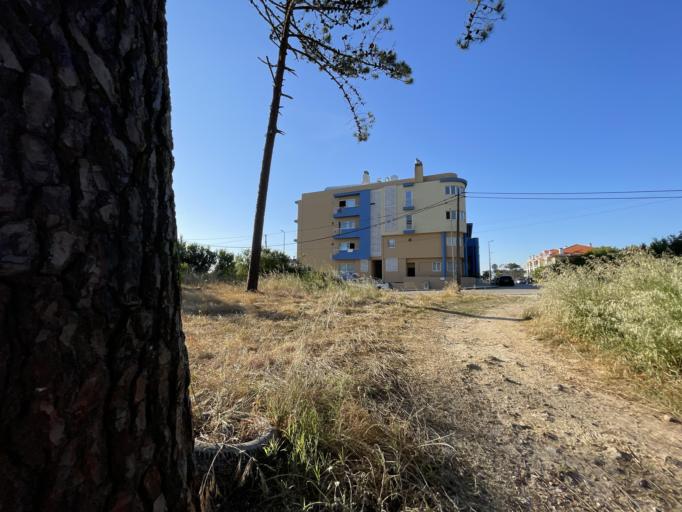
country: PT
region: Aveiro
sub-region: Ovar
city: Esmoriz
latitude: 40.9401
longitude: -8.6551
